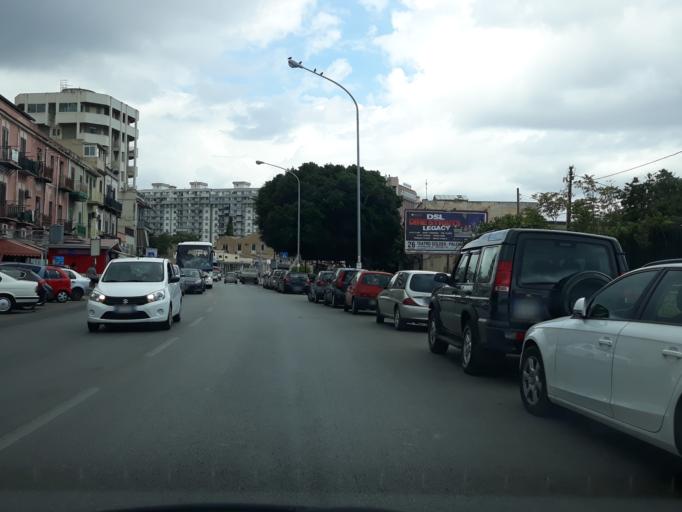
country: IT
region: Sicily
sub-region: Palermo
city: Ciaculli
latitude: 38.1066
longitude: 13.3849
